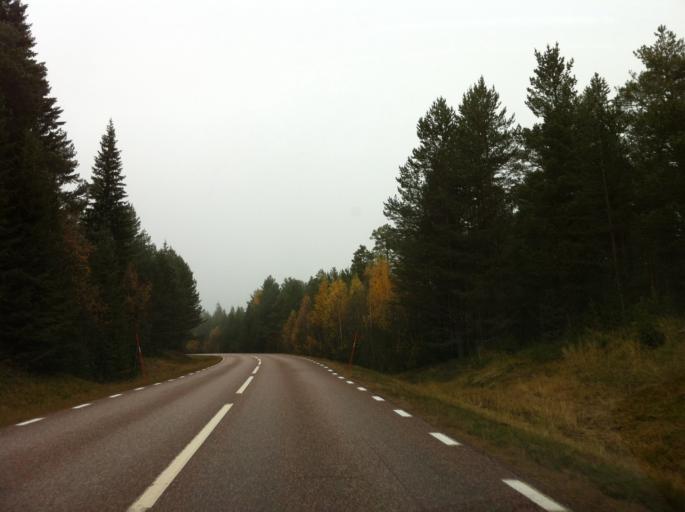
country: NO
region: Hedmark
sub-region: Trysil
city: Innbygda
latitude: 61.7428
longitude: 12.9757
